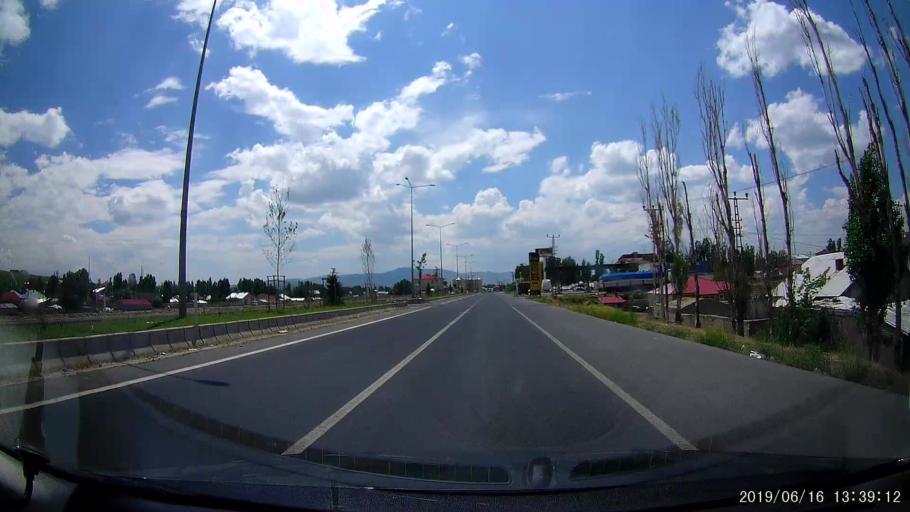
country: TR
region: Agri
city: Agri
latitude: 39.7090
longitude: 43.0619
